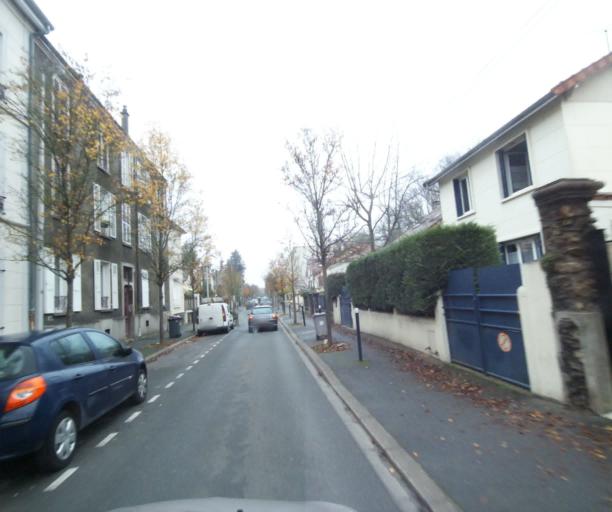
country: FR
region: Ile-de-France
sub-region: Departement de Seine-Saint-Denis
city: Gagny
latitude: 48.8829
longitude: 2.5243
